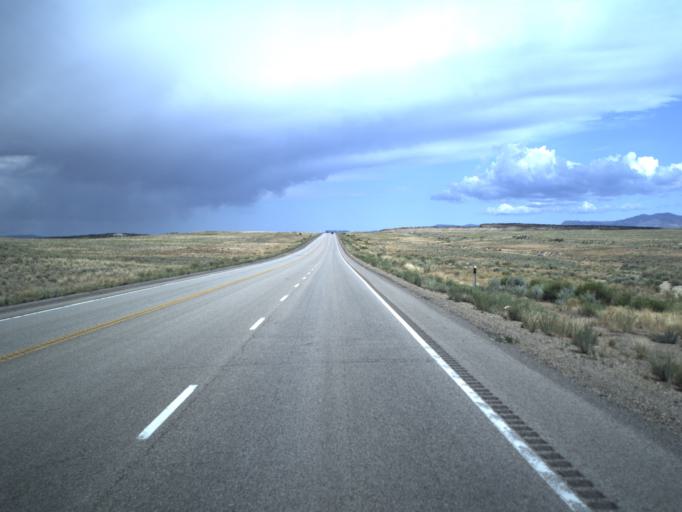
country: US
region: Utah
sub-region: Carbon County
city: Wellington
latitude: 39.5302
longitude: -110.5837
